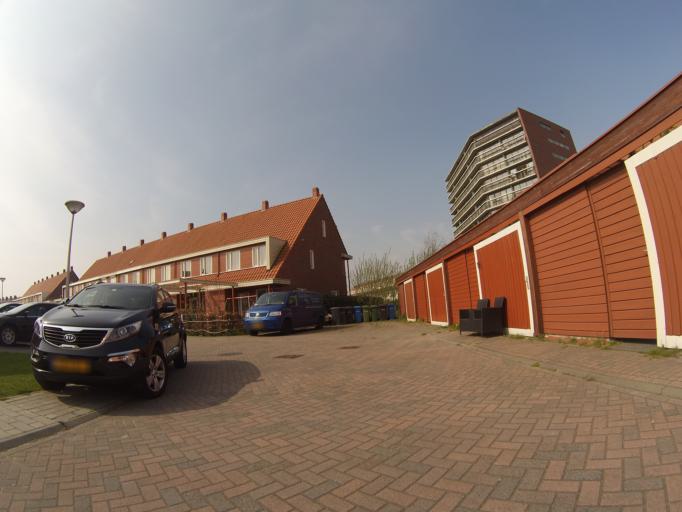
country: NL
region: Utrecht
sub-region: Gemeente Amersfoort
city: Amersfoort
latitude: 52.1648
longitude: 5.3928
